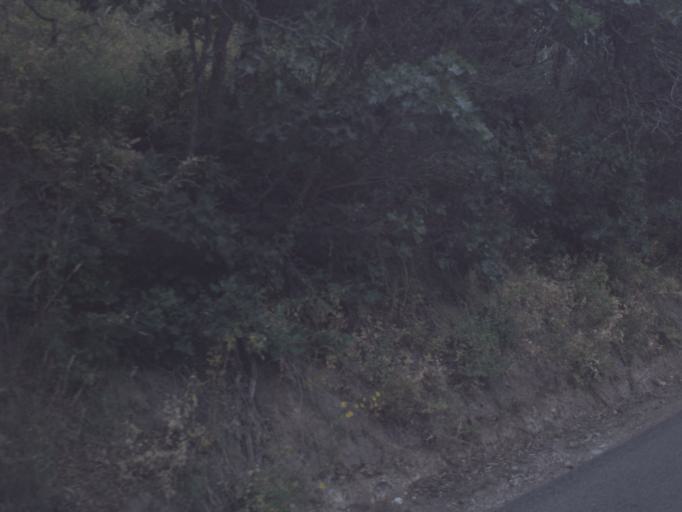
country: US
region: Utah
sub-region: Utah County
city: Lindon
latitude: 40.4399
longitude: -111.6206
